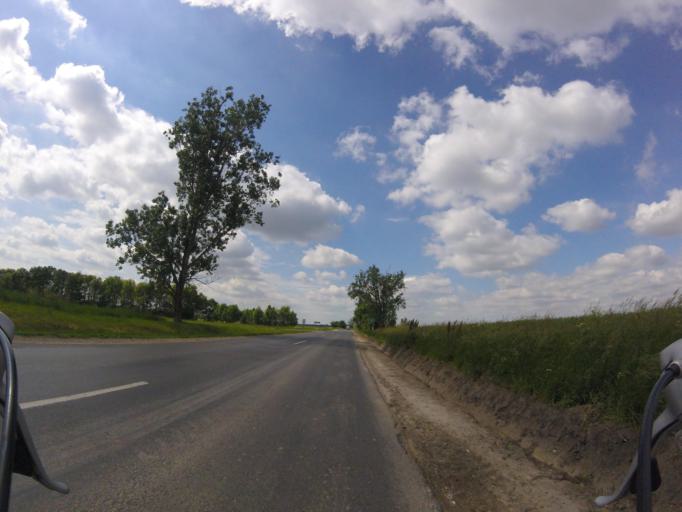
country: HU
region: Fejer
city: Soponya
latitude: 47.0441
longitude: 18.4298
